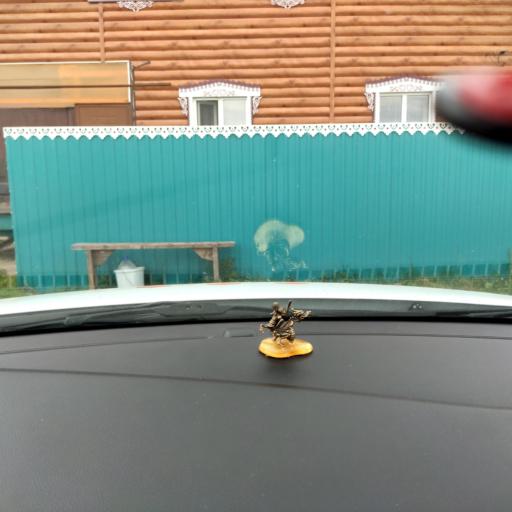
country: RU
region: Tatarstan
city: Kuybyshevskiy Zaton
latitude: 55.2828
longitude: 49.3474
